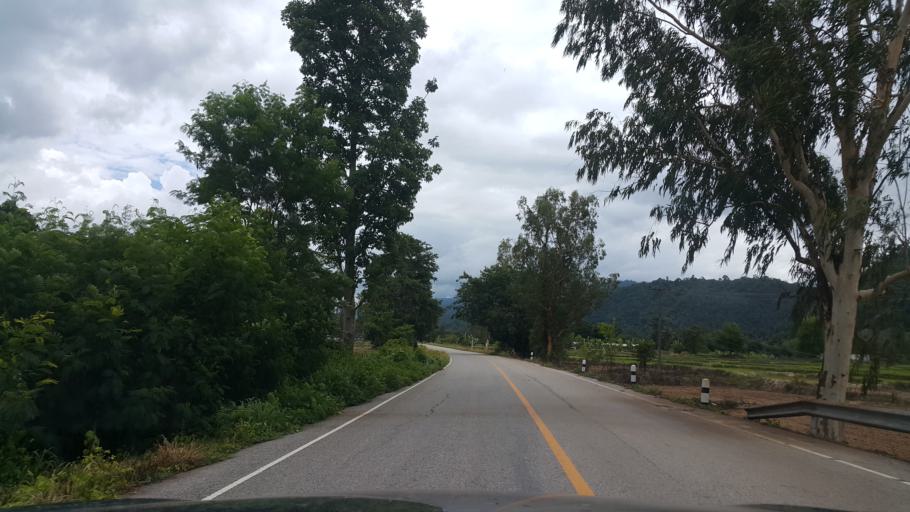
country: TH
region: Phitsanulok
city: Chat Trakan
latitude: 17.3783
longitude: 100.7499
